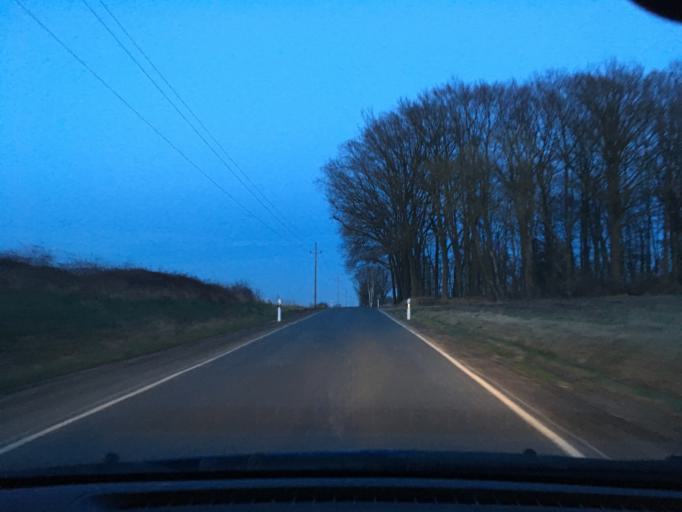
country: DE
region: Lower Saxony
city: Eyendorf
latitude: 53.2016
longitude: 10.1704
